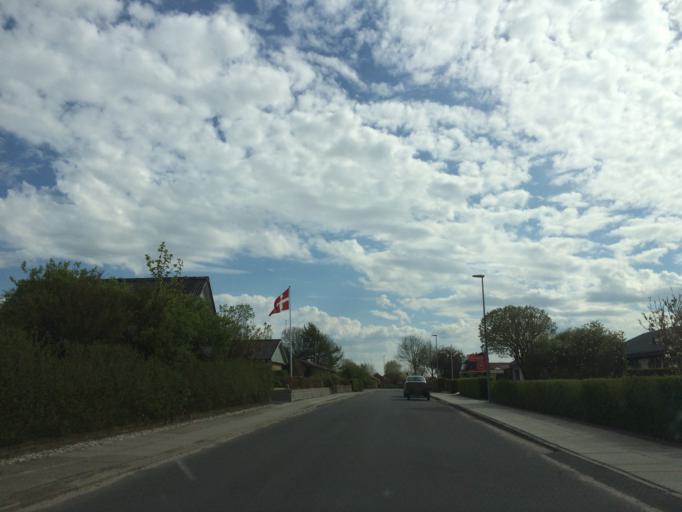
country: DK
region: Central Jutland
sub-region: Viborg Kommune
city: Bjerringbro
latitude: 56.2658
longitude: 9.7299
